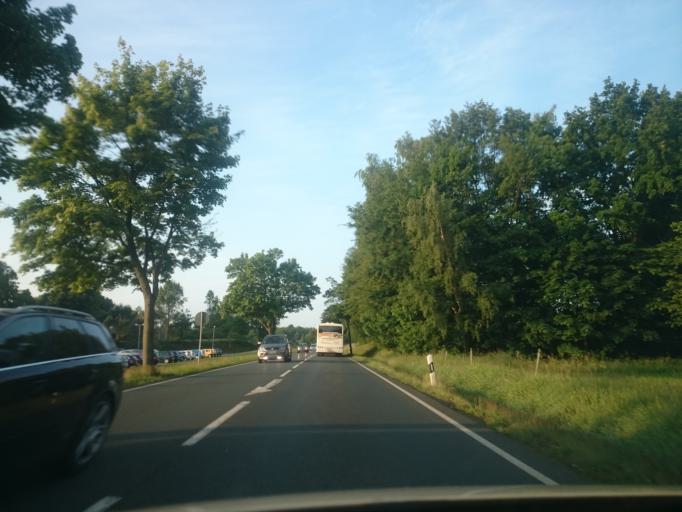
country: DE
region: Saxony
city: Brand-Erbisdorf
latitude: 50.8539
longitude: 13.3203
